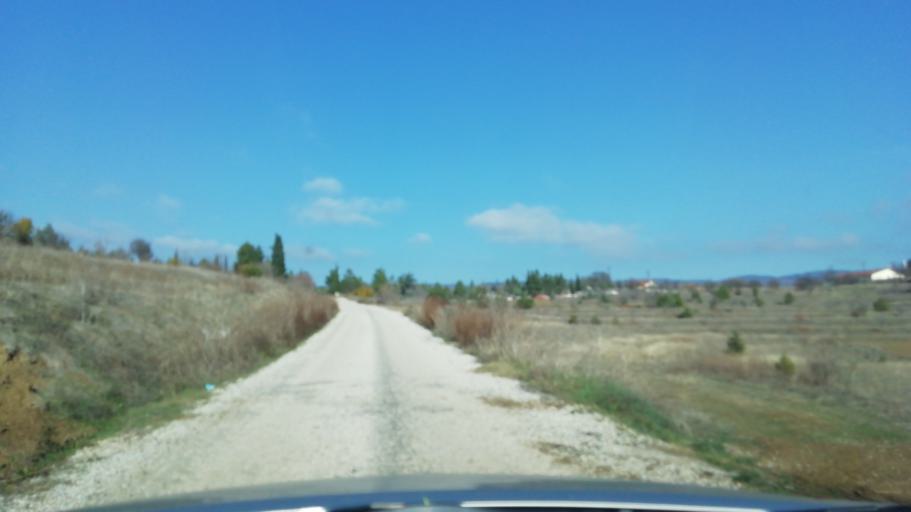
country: TR
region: Karabuk
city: Safranbolu
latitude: 41.2281
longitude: 32.7763
